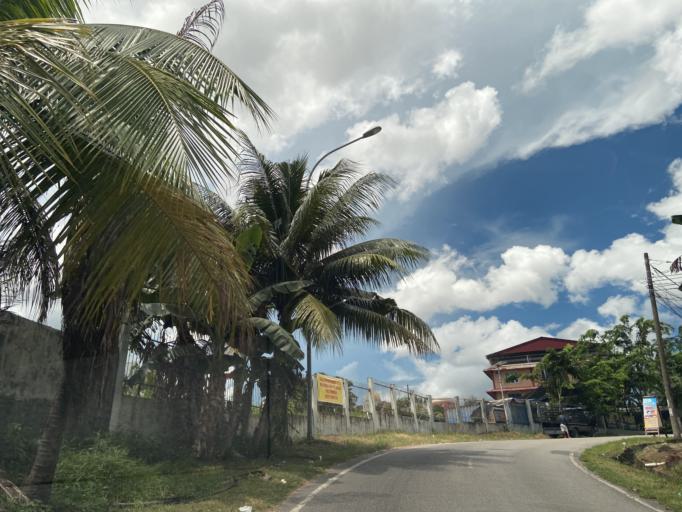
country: SG
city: Singapore
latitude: 1.1366
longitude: 104.0139
